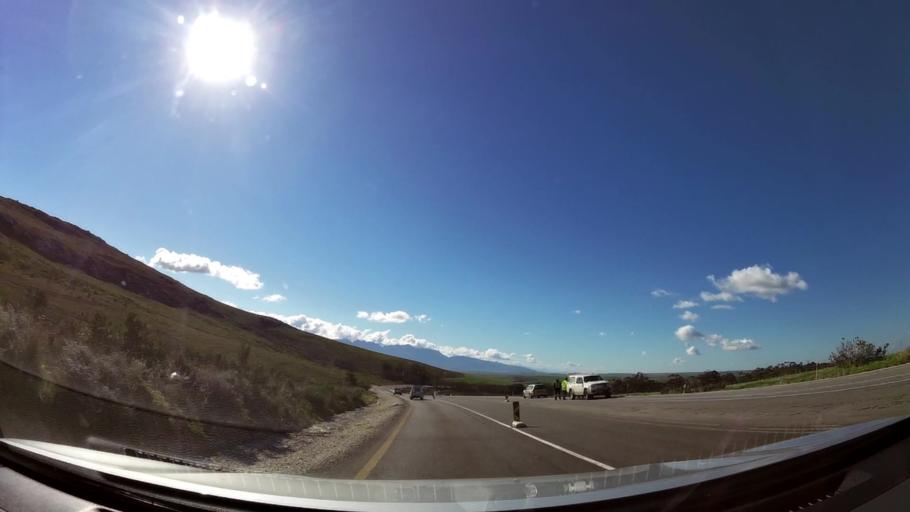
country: ZA
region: Western Cape
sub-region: Overberg District Municipality
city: Caledon
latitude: -34.2067
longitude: 19.5870
